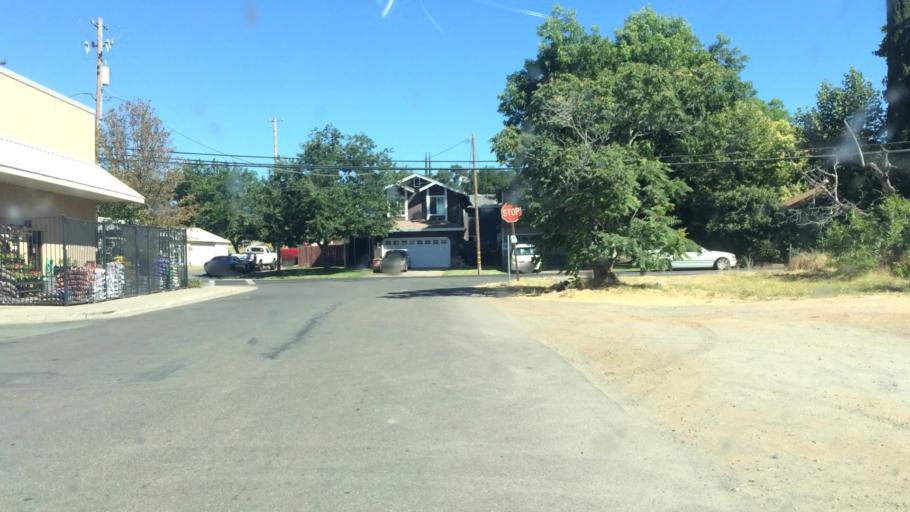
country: US
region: California
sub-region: Amador County
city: Ione
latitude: 38.3535
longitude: -120.9364
